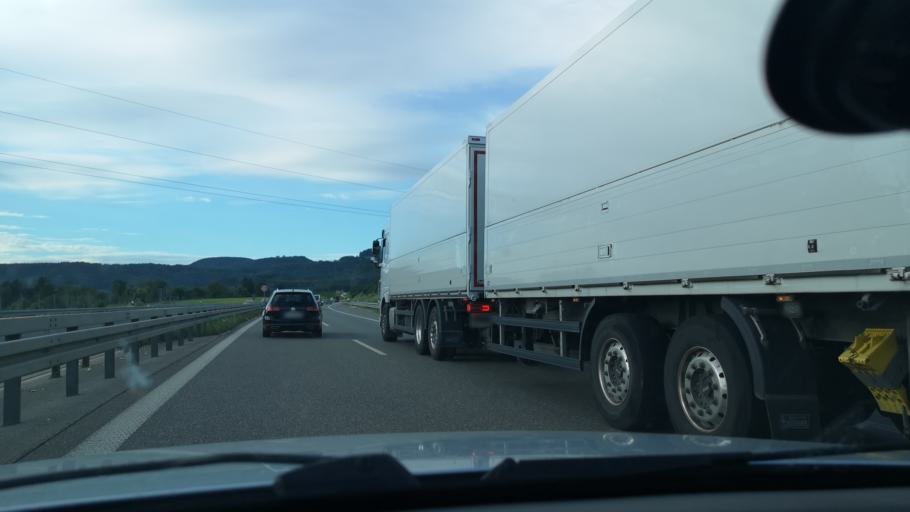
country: DE
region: Baden-Wuerttemberg
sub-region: Regierungsbezirk Stuttgart
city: Salach
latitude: 48.6769
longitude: 9.7255
